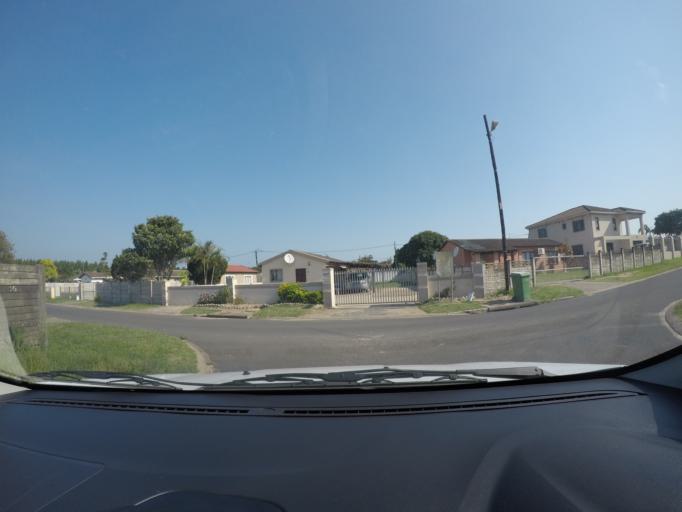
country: ZA
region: KwaZulu-Natal
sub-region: uThungulu District Municipality
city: Richards Bay
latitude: -28.7179
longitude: 32.0441
